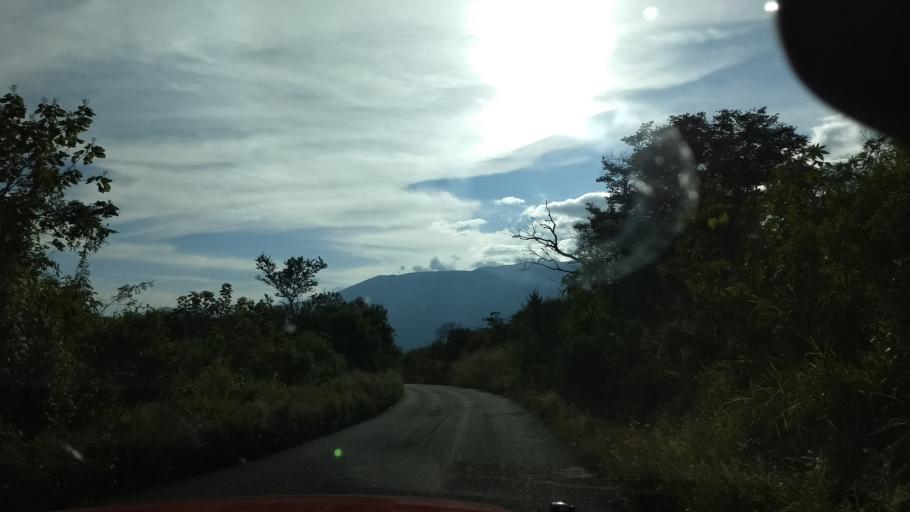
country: MX
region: Colima
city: Suchitlan
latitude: 19.4645
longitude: -103.7842
